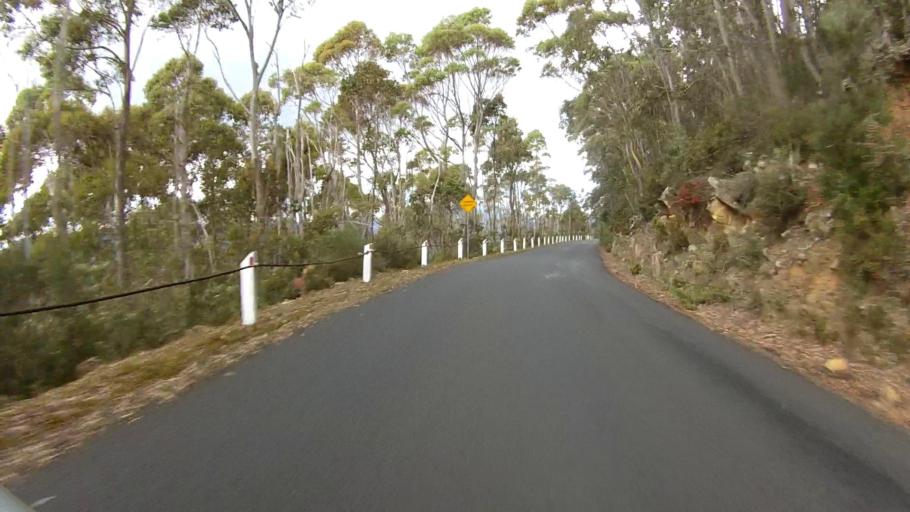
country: AU
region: Tasmania
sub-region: Glenorchy
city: West Moonah
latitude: -42.8938
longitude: 147.2445
